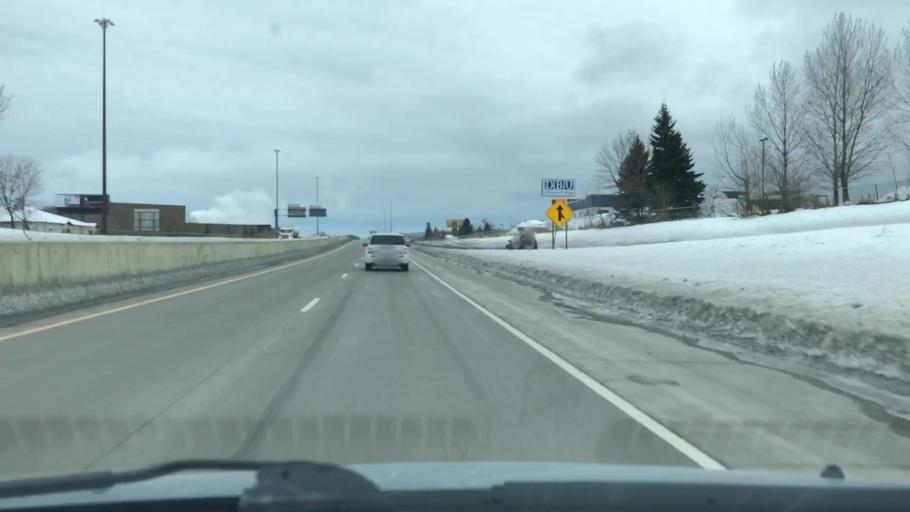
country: US
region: Wisconsin
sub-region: Douglas County
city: Superior
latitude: 46.7422
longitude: -92.1556
